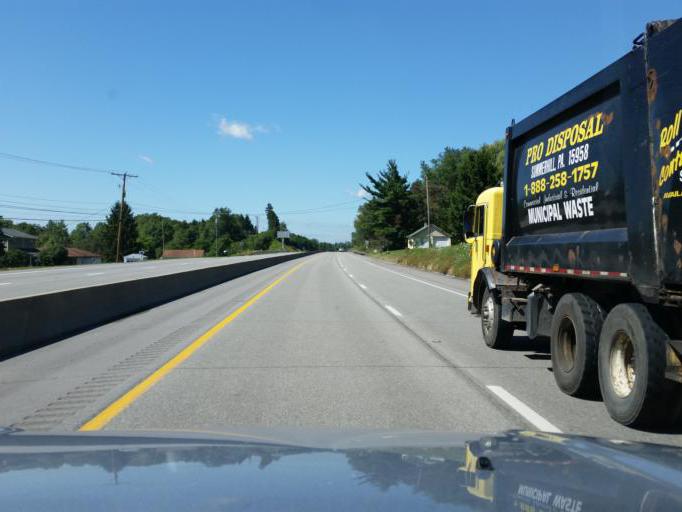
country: US
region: Pennsylvania
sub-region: Cambria County
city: Nanty Glo
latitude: 40.4515
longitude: -78.7867
